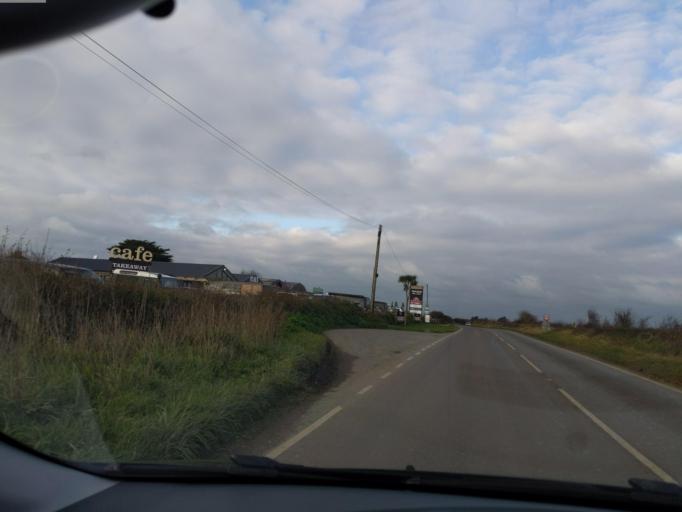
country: GB
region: England
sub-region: Cornwall
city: Padstow
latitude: 50.5182
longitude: -4.9507
